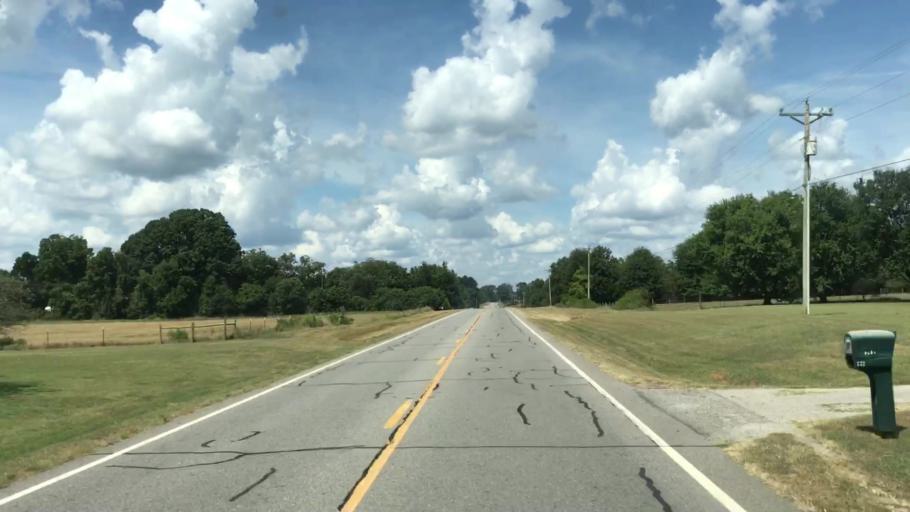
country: US
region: Georgia
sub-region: Oconee County
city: Watkinsville
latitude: 33.8291
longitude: -83.3755
